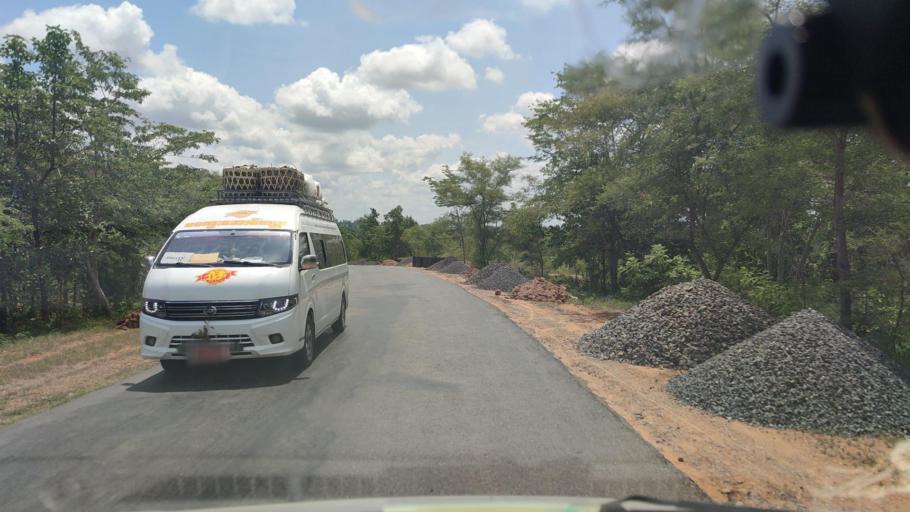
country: MM
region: Magway
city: Magway
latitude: 20.1878
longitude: 95.1371
